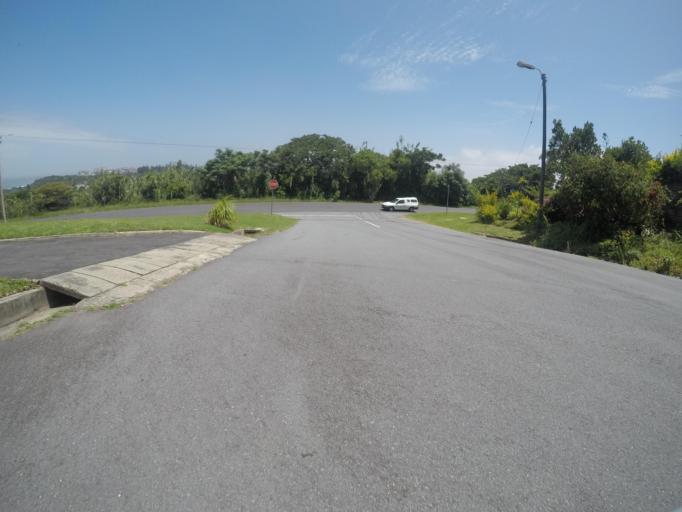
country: ZA
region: Eastern Cape
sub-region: Buffalo City Metropolitan Municipality
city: East London
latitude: -33.0000
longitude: 27.9249
